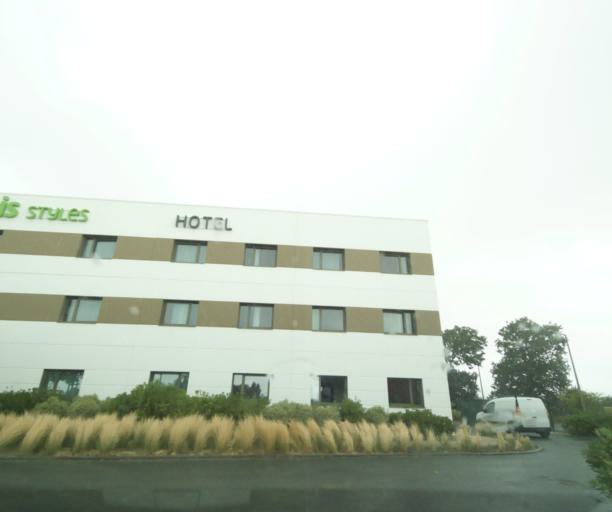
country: FR
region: Pays de la Loire
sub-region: Departement de la Vendee
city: Les Sables-d'Olonne
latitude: 46.5141
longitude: -1.7703
